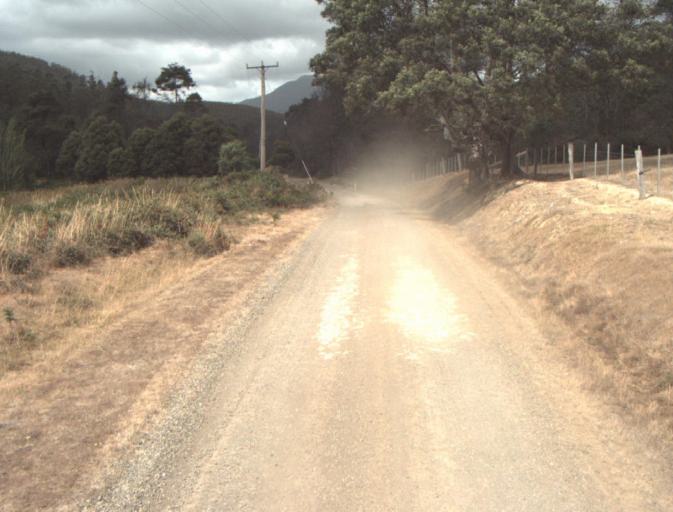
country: AU
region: Tasmania
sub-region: Dorset
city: Bridport
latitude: -41.1902
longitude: 147.2619
